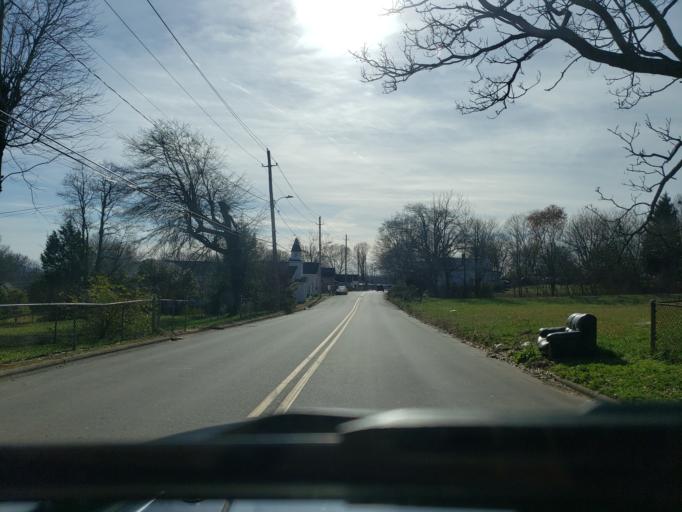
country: US
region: North Carolina
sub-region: Cleveland County
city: Kings Mountain
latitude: 35.2543
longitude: -81.3334
